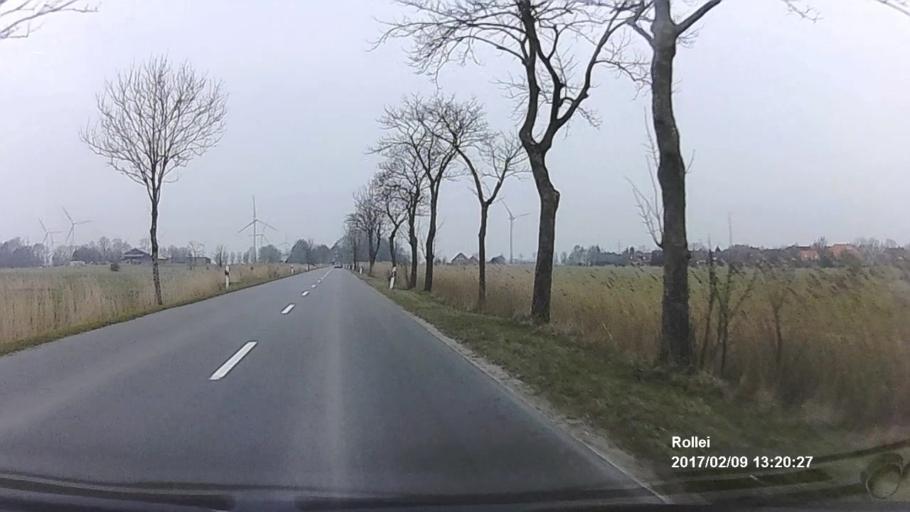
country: DE
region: Lower Saxony
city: Hinte
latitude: 53.4426
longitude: 7.1554
